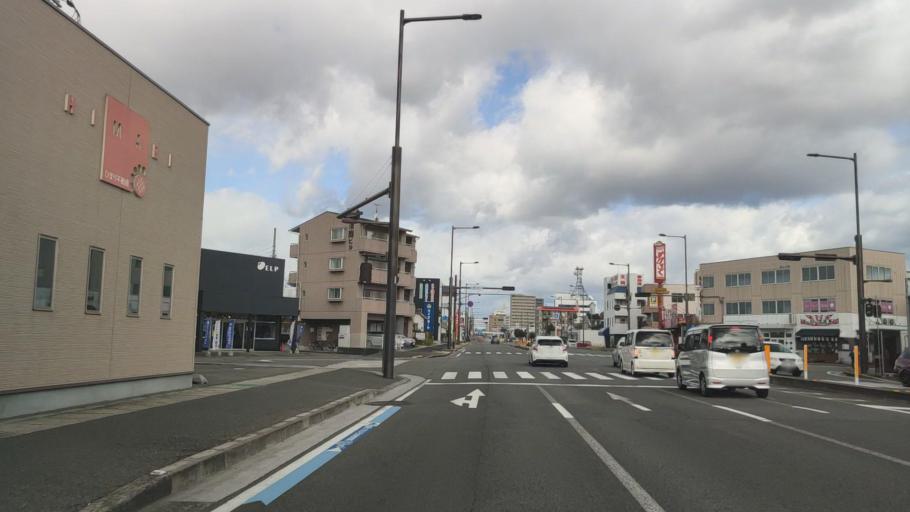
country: JP
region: Ehime
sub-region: Shikoku-chuo Shi
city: Matsuyama
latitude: 33.8276
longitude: 132.7588
